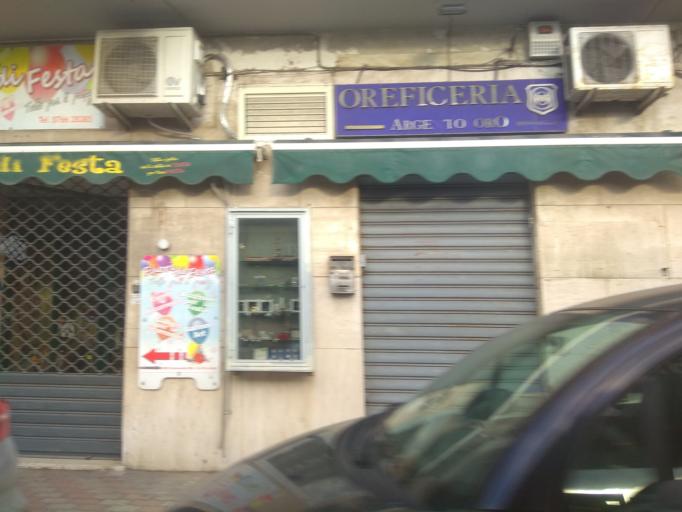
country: IT
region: Latium
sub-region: Citta metropolitana di Roma Capitale
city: Civitavecchia
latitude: 42.0949
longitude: 11.7900
